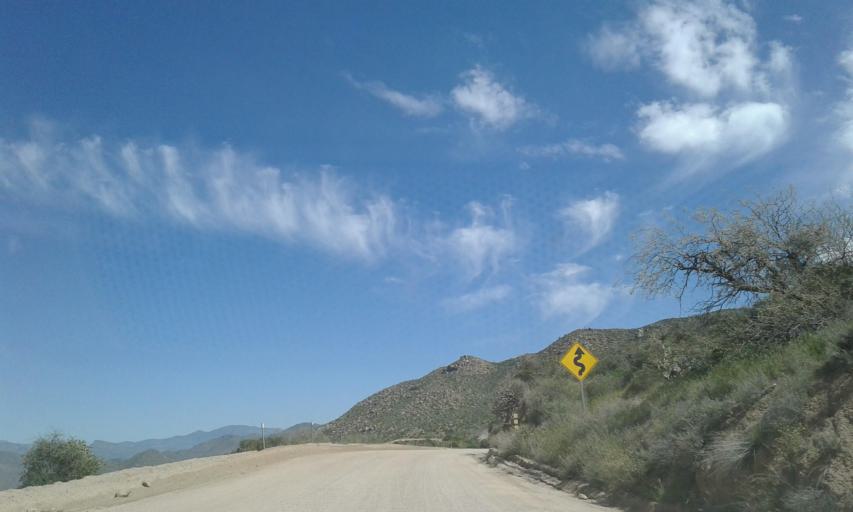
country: US
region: Arizona
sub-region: Gila County
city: Tonto Basin
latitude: 33.5657
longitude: -111.2383
